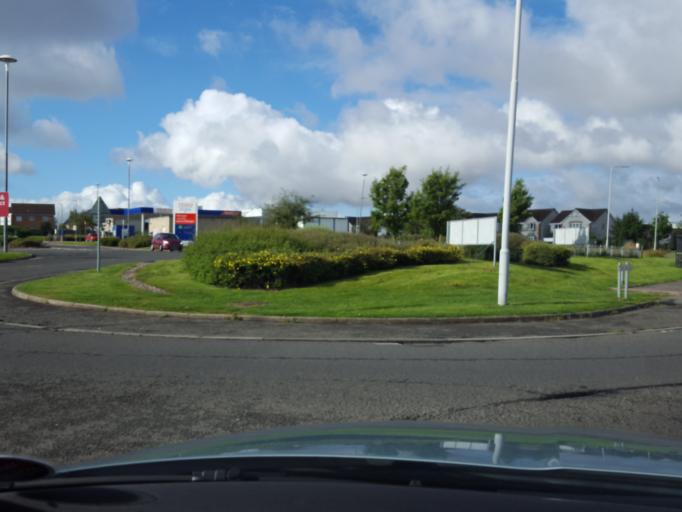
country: GB
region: Scotland
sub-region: Fife
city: Crossgates
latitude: 56.0612
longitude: -3.4052
